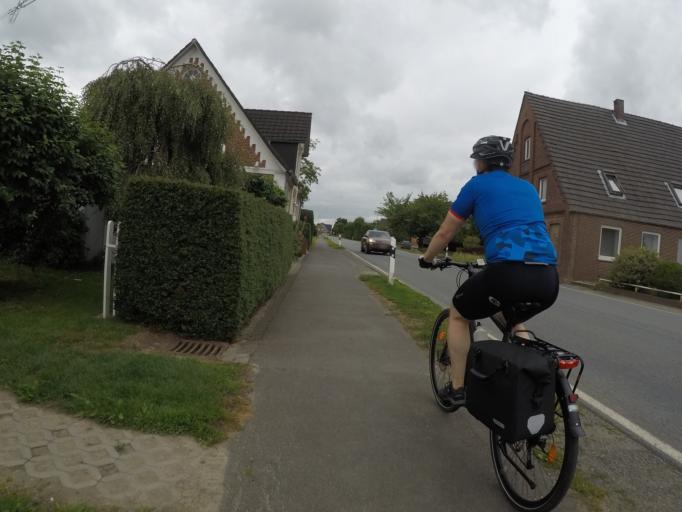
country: DE
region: Schleswig-Holstein
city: Haseldorf
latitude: 53.5874
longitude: 9.5813
